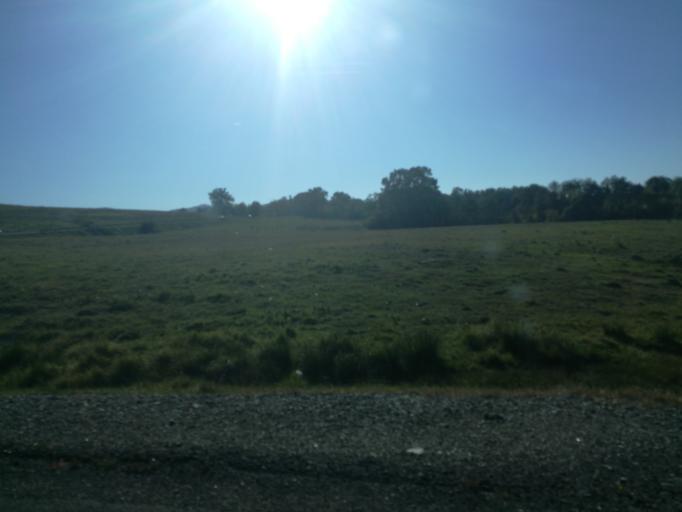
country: RO
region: Brasov
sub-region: Comuna Dumbravita
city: Dumbravita
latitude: 45.7570
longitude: 25.4004
